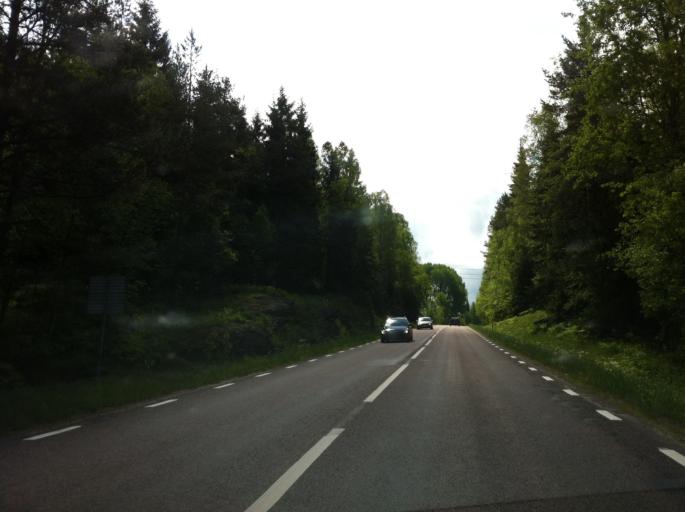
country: SE
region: Vaermland
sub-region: Karlstads Kommun
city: Edsvalla
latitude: 59.5527
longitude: 13.1916
